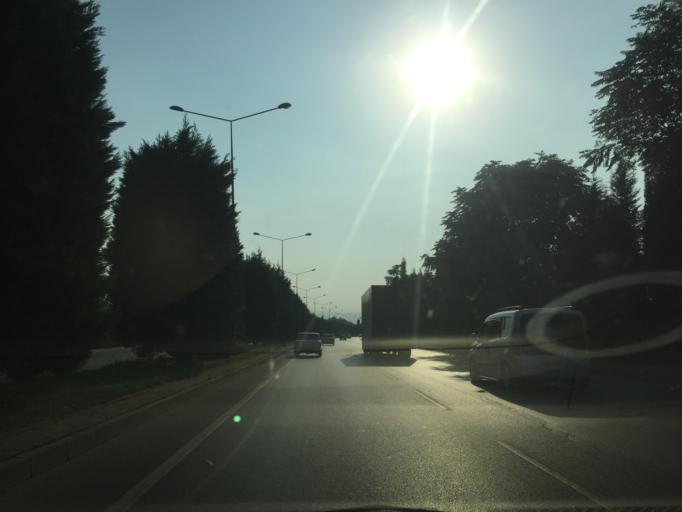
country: TR
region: Manisa
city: Salihli
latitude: 38.4902
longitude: 28.1599
